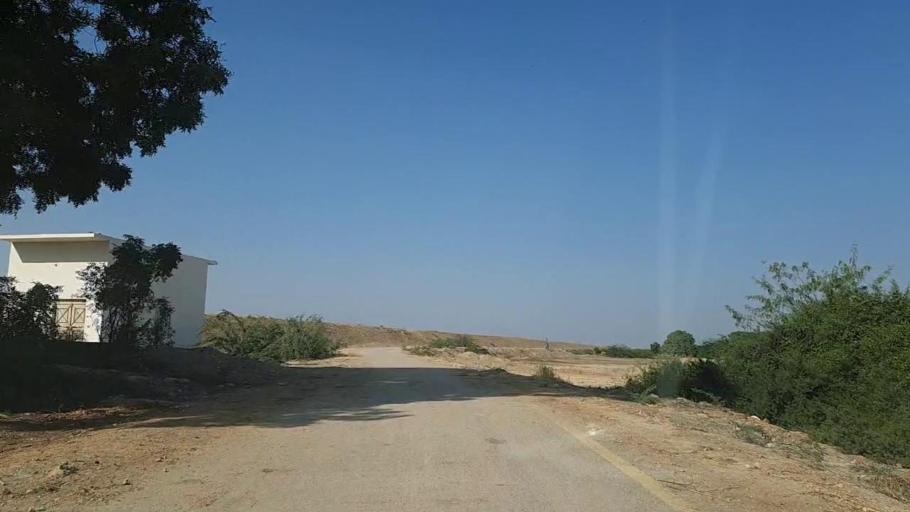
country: PK
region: Sindh
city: Chuhar Jamali
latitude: 24.5583
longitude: 68.0280
